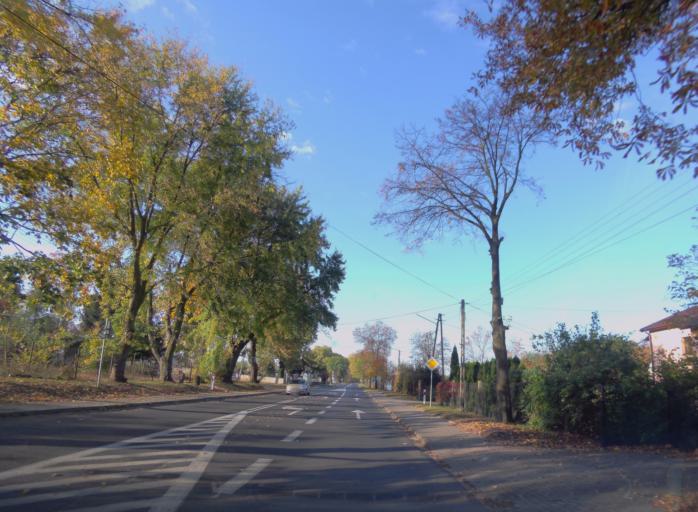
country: PL
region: Masovian Voivodeship
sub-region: Powiat siedlecki
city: Mordy
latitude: 52.2062
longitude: 22.5153
